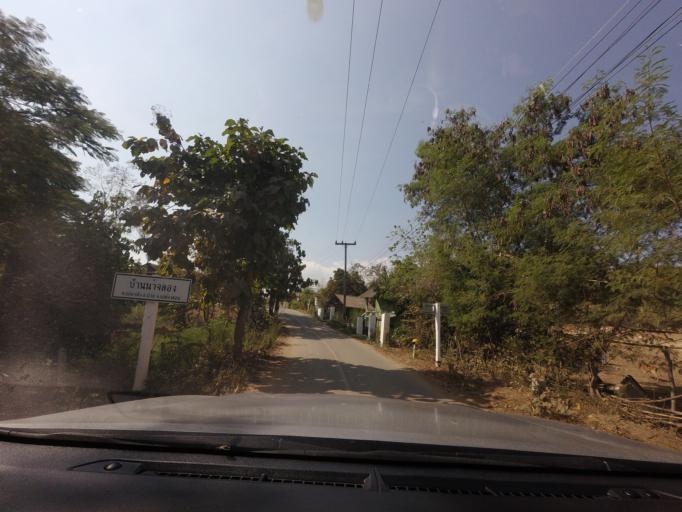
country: TH
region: Mae Hong Son
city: Wiang Nuea
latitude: 19.4024
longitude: 98.4447
